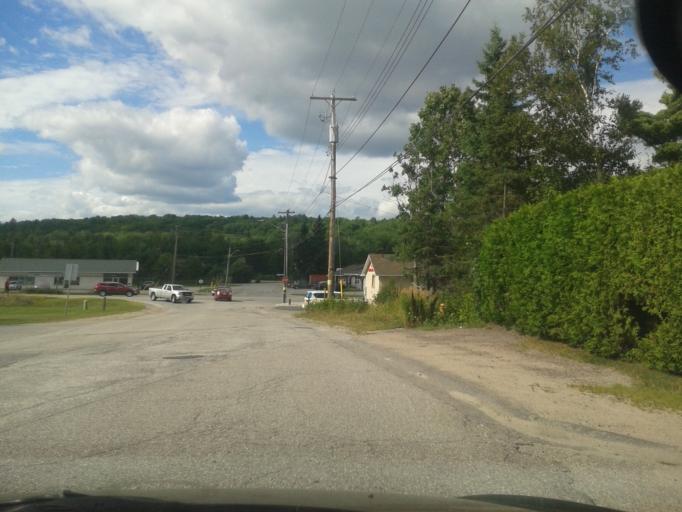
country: CA
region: Ontario
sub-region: Nipissing District
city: North Bay
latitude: 46.3340
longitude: -79.4631
